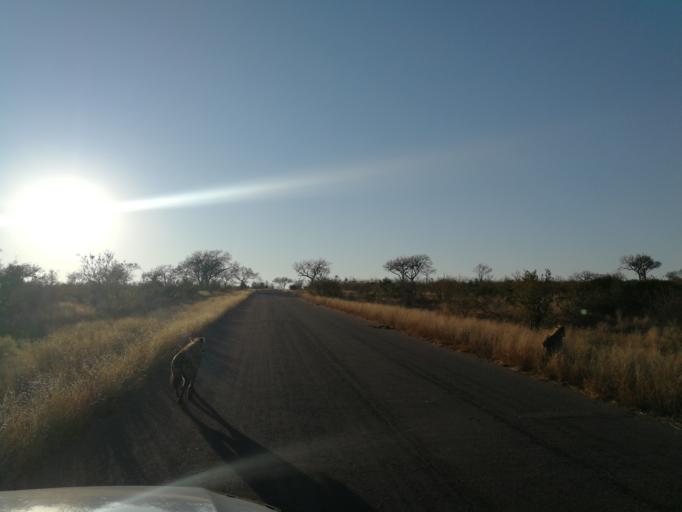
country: ZA
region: Limpopo
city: Thulamahashi
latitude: -25.0288
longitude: 31.3629
